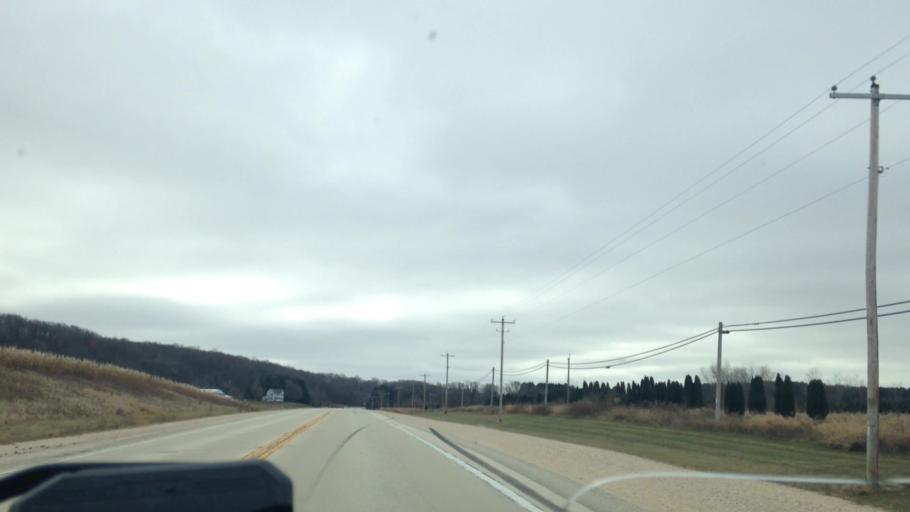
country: US
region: Wisconsin
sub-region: Dodge County
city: Mayville
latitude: 43.4637
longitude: -88.5456
